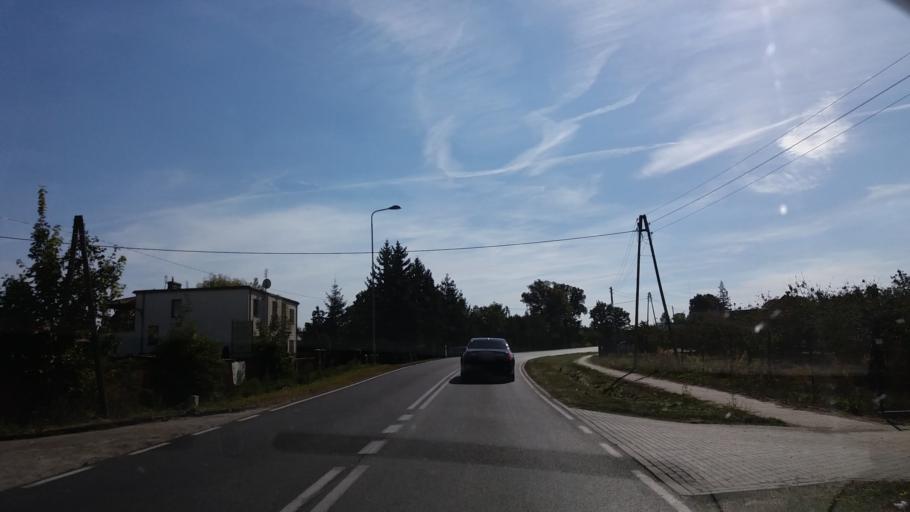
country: PL
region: Greater Poland Voivodeship
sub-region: Powiat miedzychodzki
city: Miedzychod
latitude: 52.5786
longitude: 15.8987
